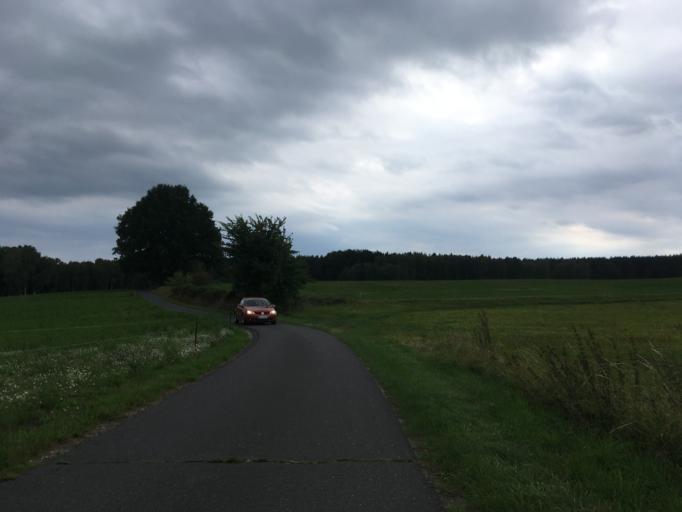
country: DE
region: Brandenburg
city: Friedrichswalde
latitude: 53.0199
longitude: 13.7313
